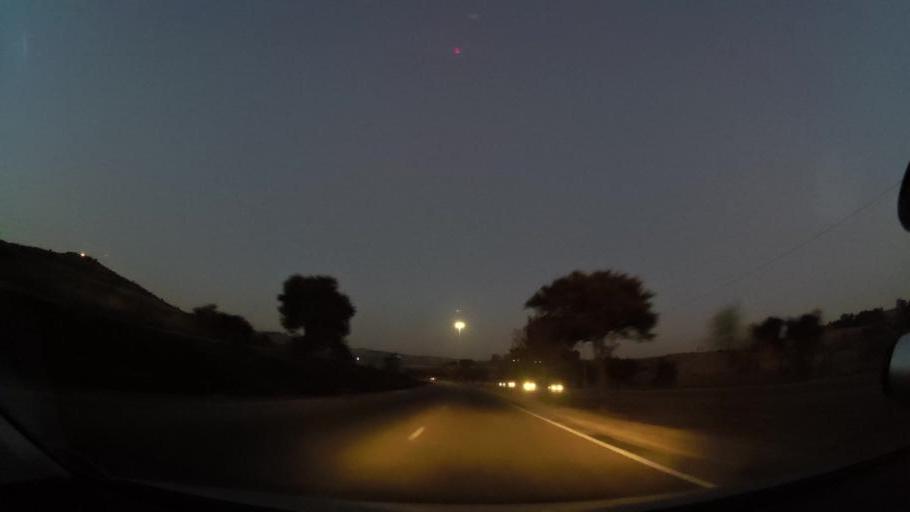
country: ZA
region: Gauteng
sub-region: City of Tshwane Metropolitan Municipality
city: Pretoria
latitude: -25.7819
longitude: 28.1756
